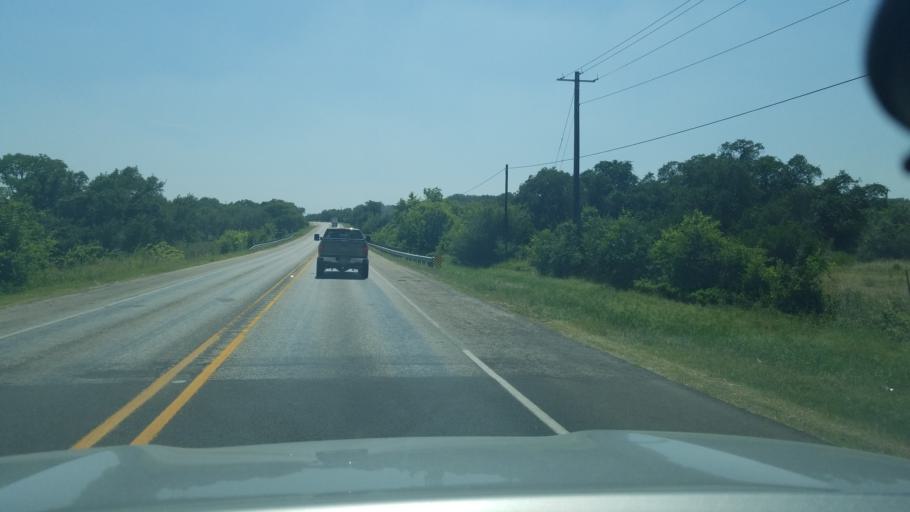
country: US
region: Texas
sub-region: Kendall County
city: Boerne
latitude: 29.7938
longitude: -98.6756
